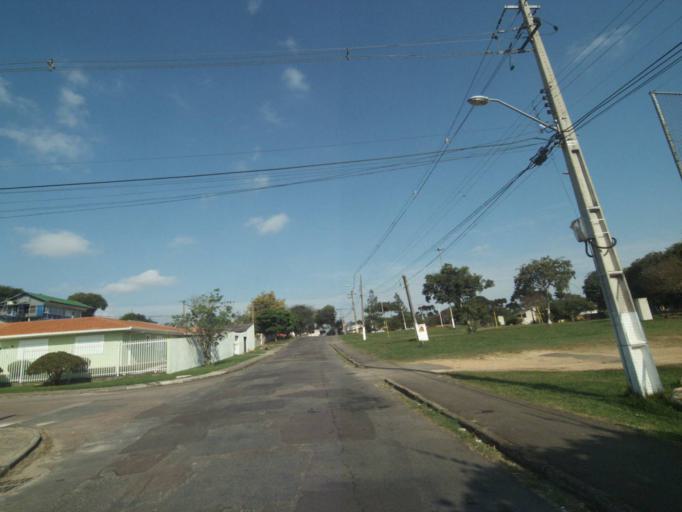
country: BR
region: Parana
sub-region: Curitiba
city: Curitiba
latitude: -25.4909
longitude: -49.3293
